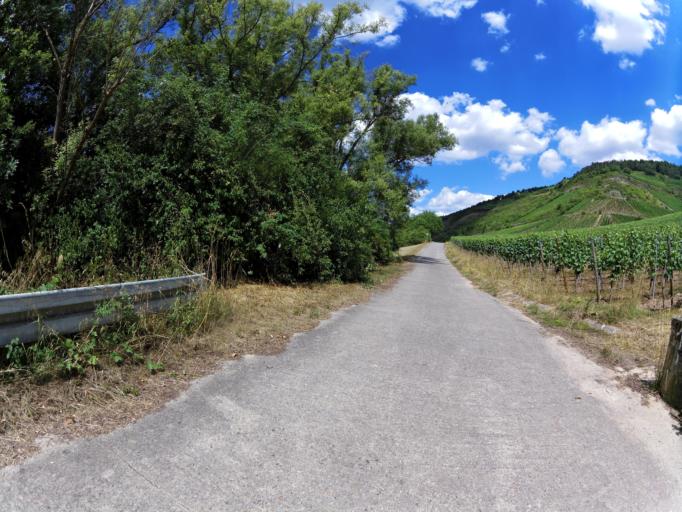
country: DE
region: Bavaria
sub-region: Regierungsbezirk Unterfranken
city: Thungersheim
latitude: 49.8901
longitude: 9.8391
